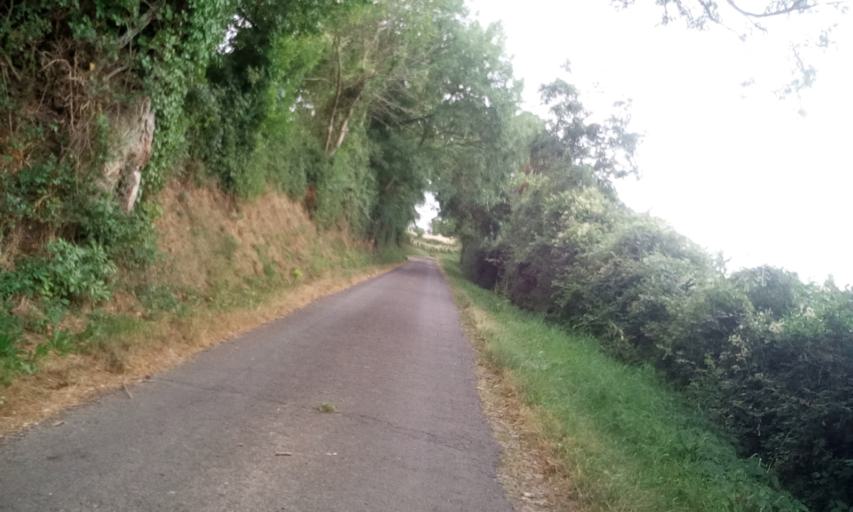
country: FR
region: Lower Normandy
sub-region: Departement du Calvados
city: Thury-Harcourt
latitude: 49.0069
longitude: -0.4408
